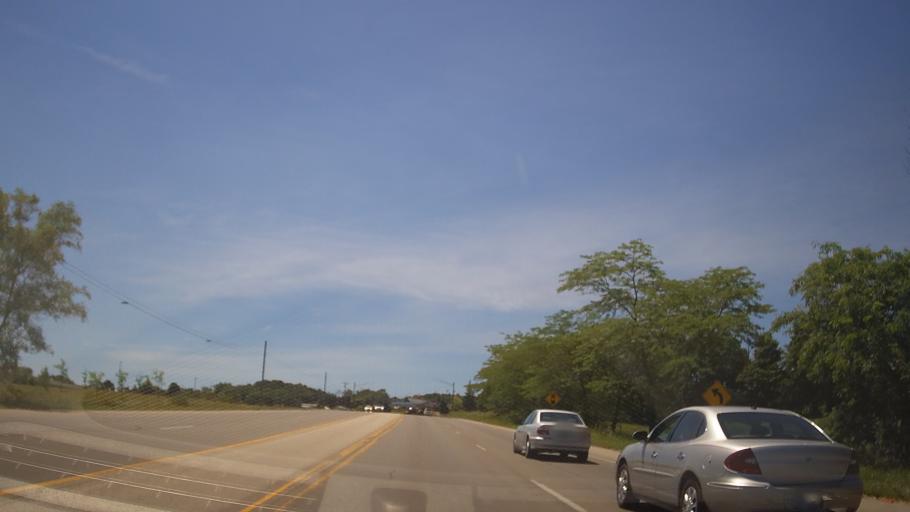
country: US
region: Michigan
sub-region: Grand Traverse County
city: Traverse City
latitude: 44.7452
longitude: -85.6510
